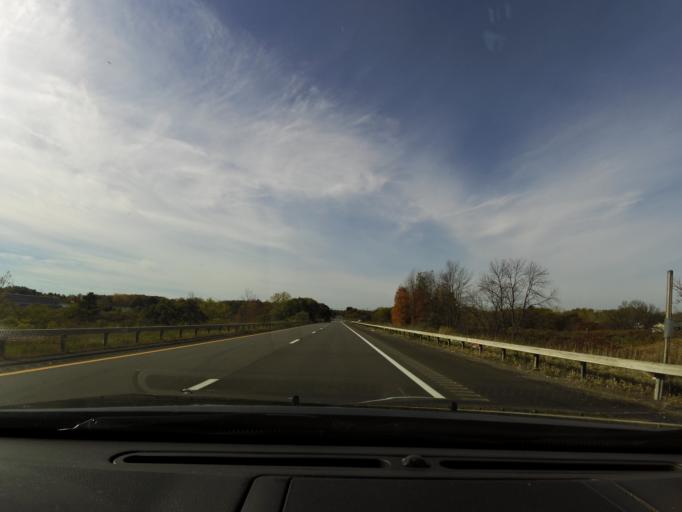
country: US
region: New York
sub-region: Erie County
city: Billington Heights
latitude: 42.7973
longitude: -78.6177
